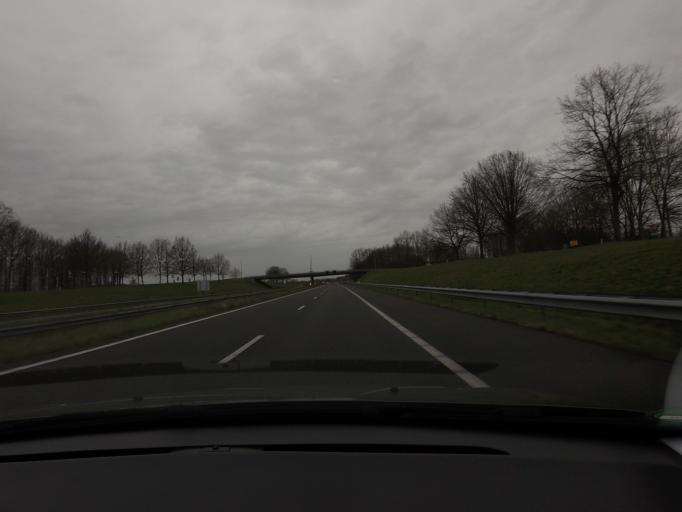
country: NL
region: Limburg
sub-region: Gemeente Maastricht
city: Heer
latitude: 50.8131
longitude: 5.7227
